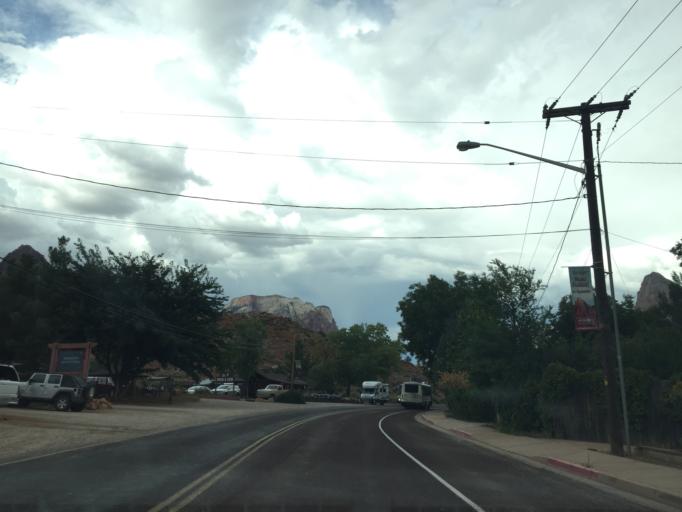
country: US
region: Utah
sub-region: Washington County
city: Hildale
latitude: 37.1809
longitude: -113.0061
